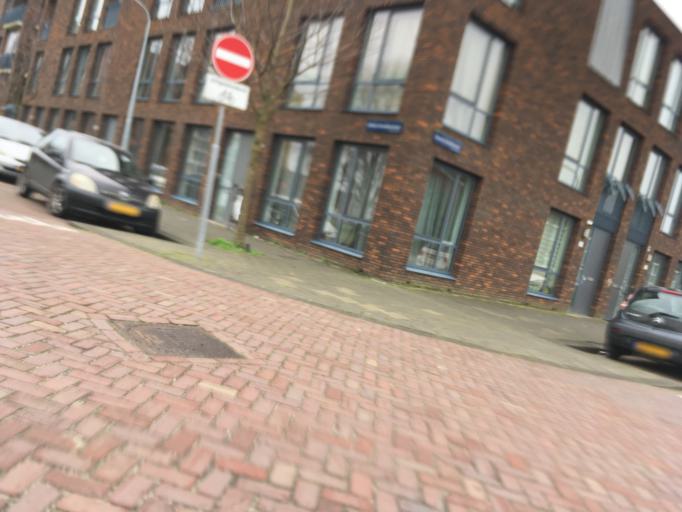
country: NL
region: North Holland
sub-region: Gemeente Haarlem
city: Haarlem
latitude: 52.3712
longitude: 4.6526
